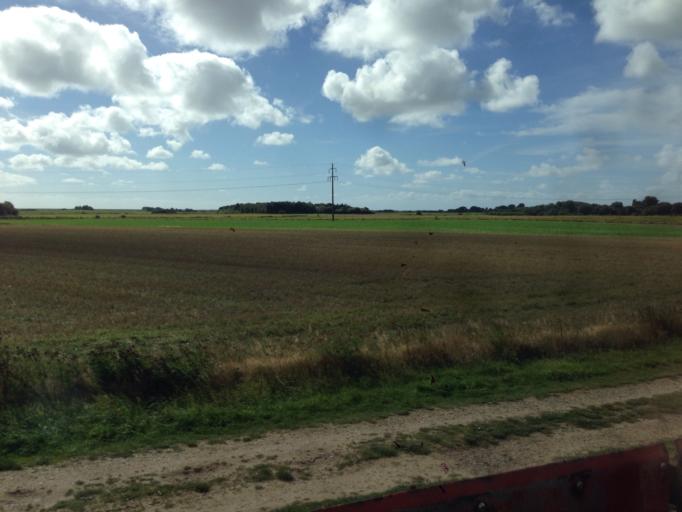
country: DE
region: Schleswig-Holstein
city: Sylt-Ost
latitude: 54.8759
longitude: 8.4098
